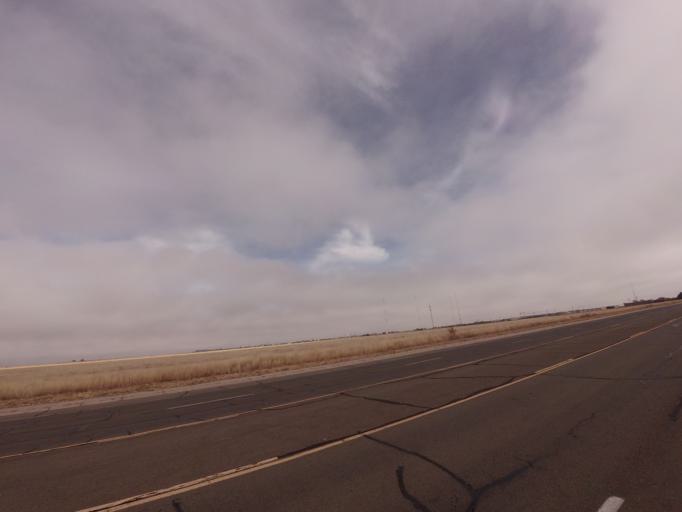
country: US
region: New Mexico
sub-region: Curry County
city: Clovis
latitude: 34.4340
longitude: -103.2189
